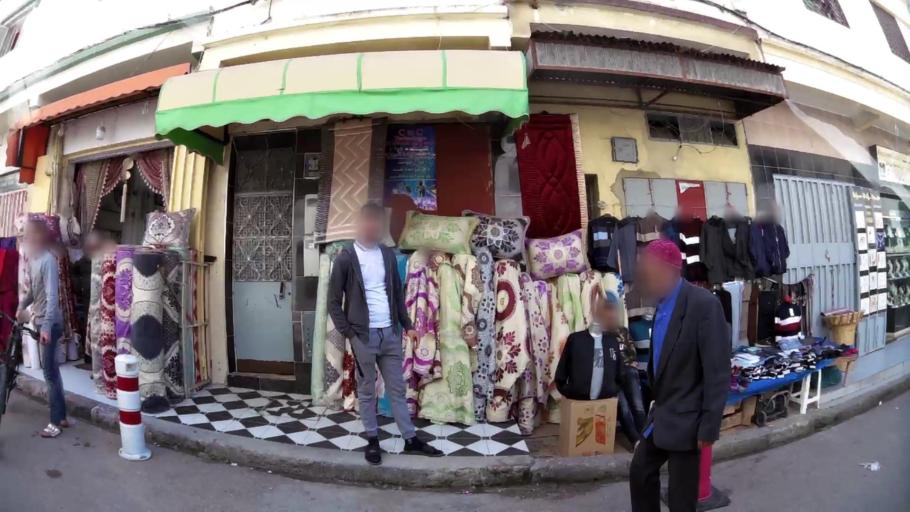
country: MA
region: Tanger-Tetouan
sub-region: Tanger-Assilah
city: Tangier
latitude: 35.7571
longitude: -5.8095
